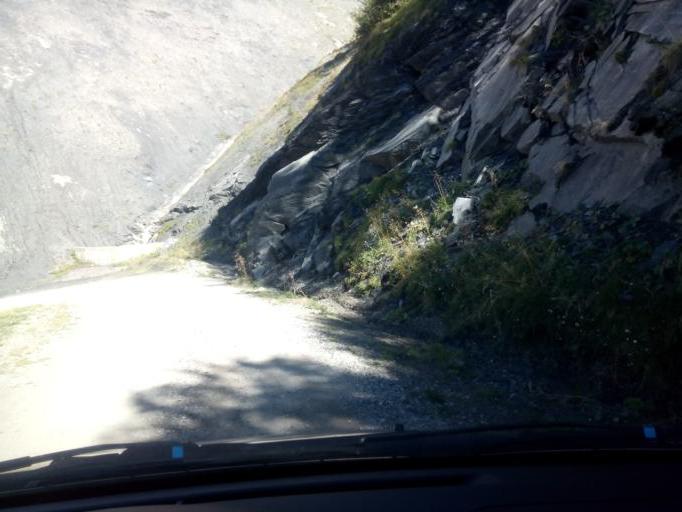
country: FR
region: Rhone-Alpes
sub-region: Departement de l'Isere
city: Mont-de-Lans
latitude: 45.0743
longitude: 6.1955
